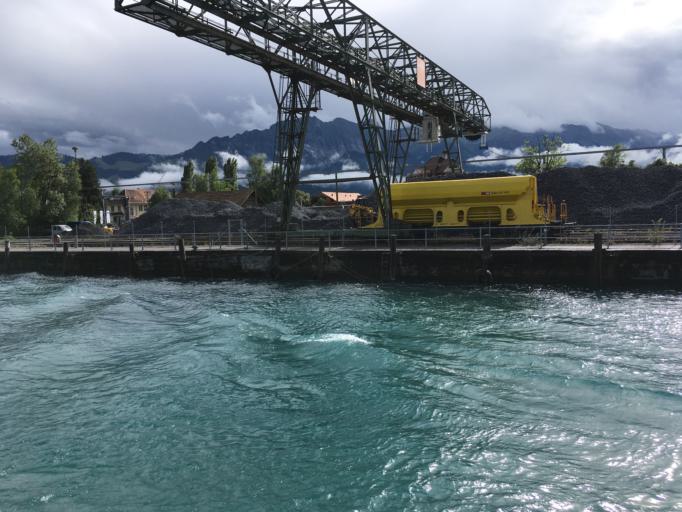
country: CH
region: Bern
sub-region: Thun District
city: Thun
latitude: 46.7497
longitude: 7.6354
